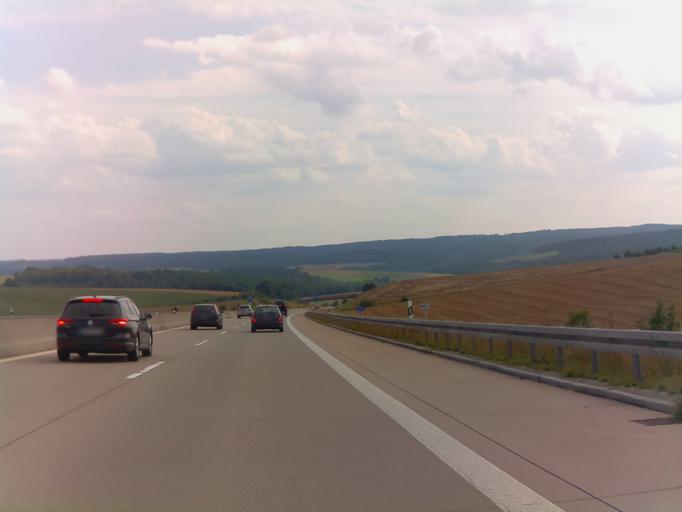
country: DE
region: Bavaria
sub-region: Regierungsbezirk Unterfranken
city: Hollstadt
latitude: 50.3628
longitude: 10.3171
